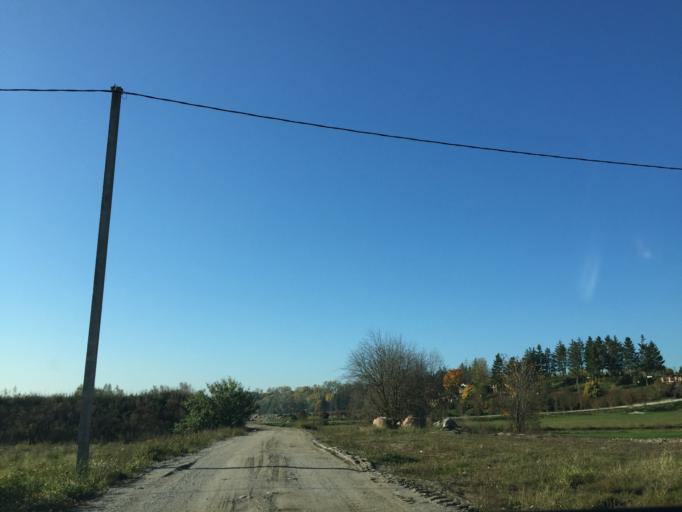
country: LT
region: Klaipedos apskritis
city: Kretinga
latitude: 55.8326
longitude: 21.1987
